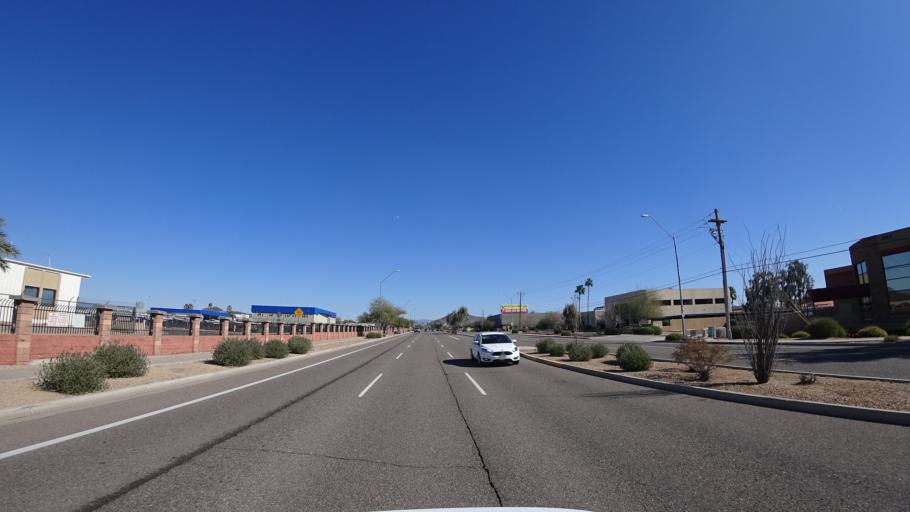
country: US
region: Arizona
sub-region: Maricopa County
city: Glendale
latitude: 33.6838
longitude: -112.0865
